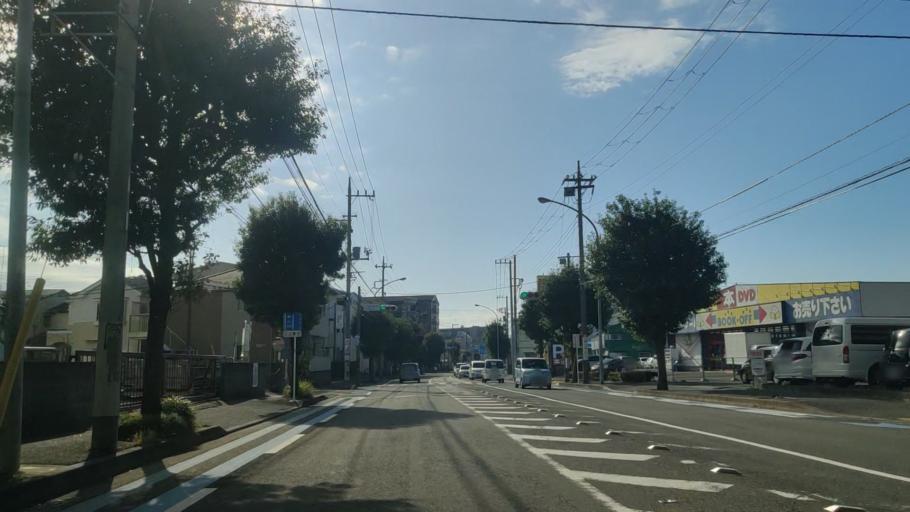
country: JP
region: Kanagawa
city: Minami-rinkan
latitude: 35.4195
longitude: 139.4853
